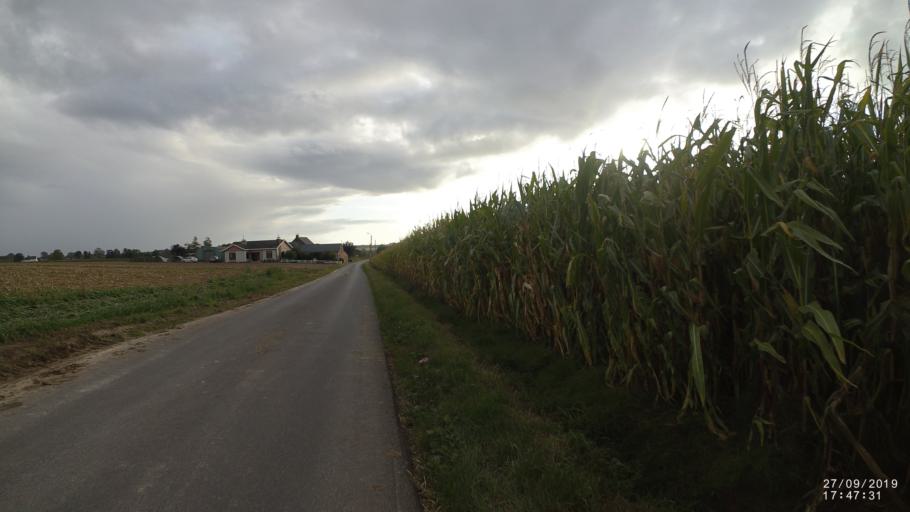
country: BE
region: Wallonia
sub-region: Province du Hainaut
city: Flobecq
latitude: 50.8290
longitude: 3.7250
